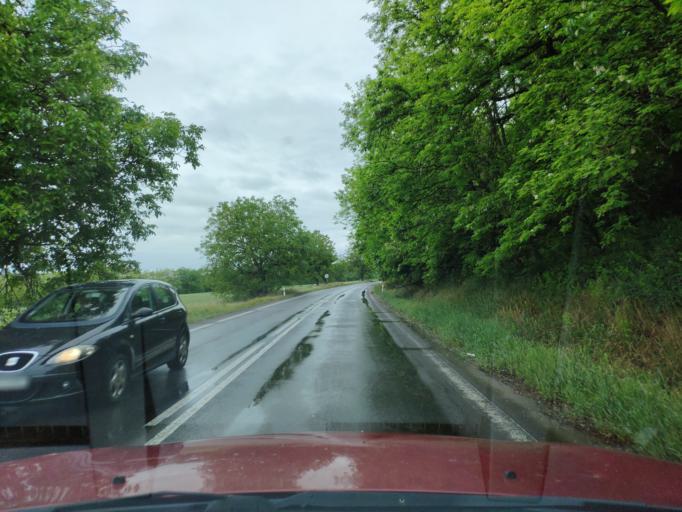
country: HU
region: Borsod-Abauj-Zemplen
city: Karcsa
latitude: 48.3912
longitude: 21.7953
